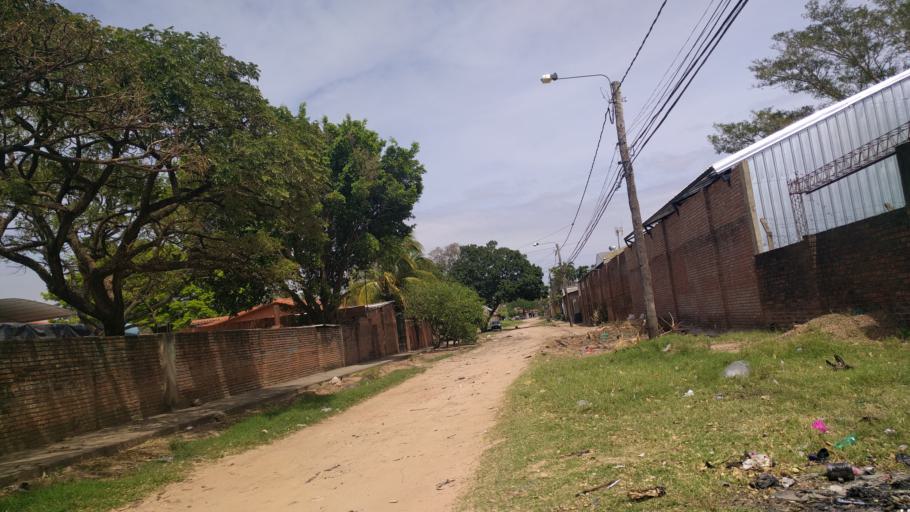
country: BO
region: Santa Cruz
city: Santa Cruz de la Sierra
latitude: -17.8159
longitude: -63.2228
